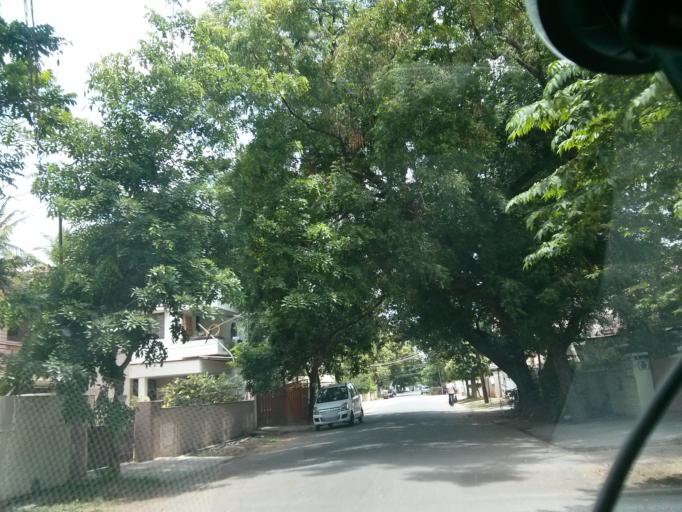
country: IN
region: Tamil Nadu
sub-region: Coimbatore
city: Coimbatore
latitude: 11.0209
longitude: 76.9412
